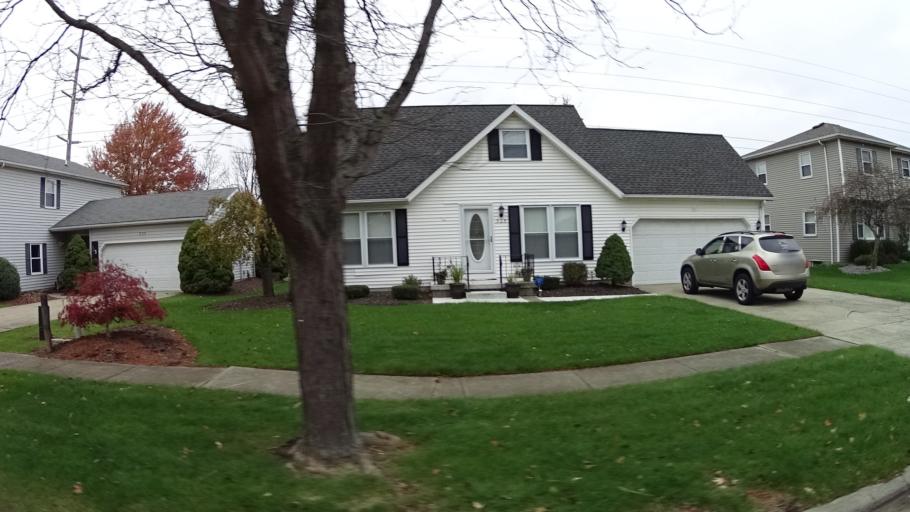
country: US
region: Ohio
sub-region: Lorain County
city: Sheffield
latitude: 41.4181
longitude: -82.0841
